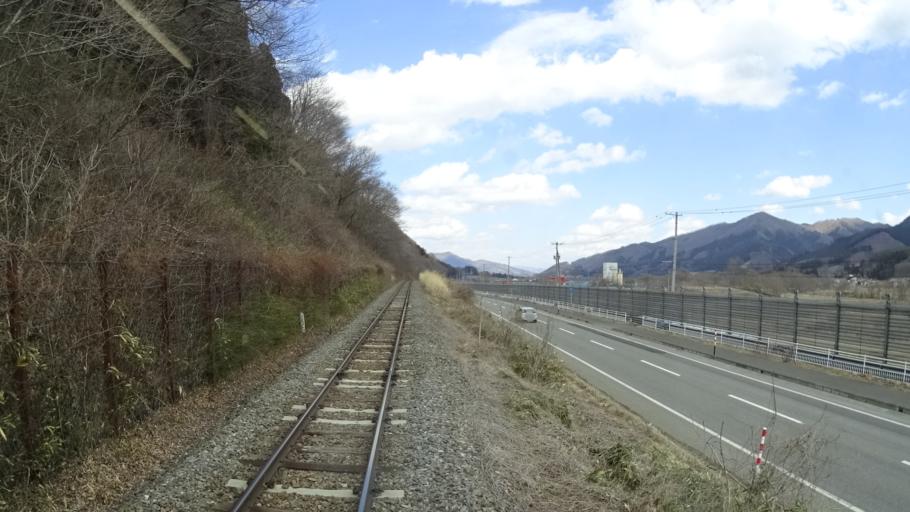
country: JP
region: Iwate
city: Tono
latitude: 39.3031
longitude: 141.4092
